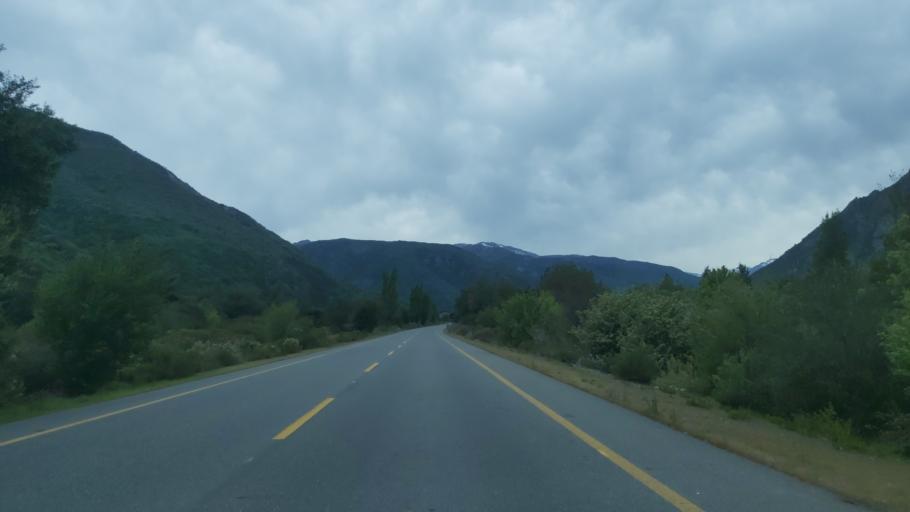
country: CL
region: Maule
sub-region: Provincia de Linares
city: Colbun
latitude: -35.7127
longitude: -71.0551
